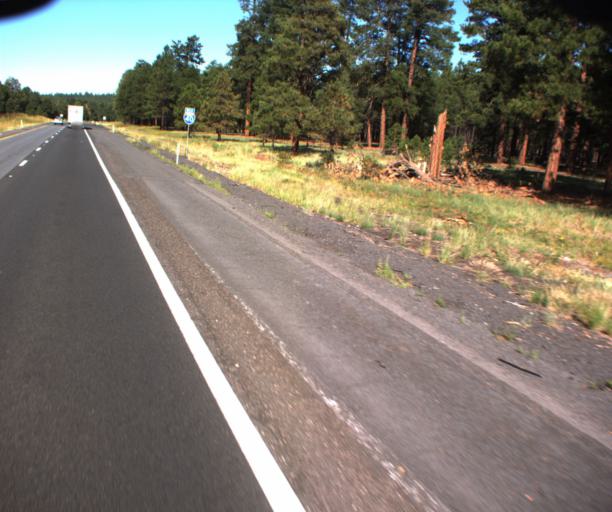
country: US
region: Arizona
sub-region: Coconino County
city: Parks
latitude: 35.2481
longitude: -111.8769
